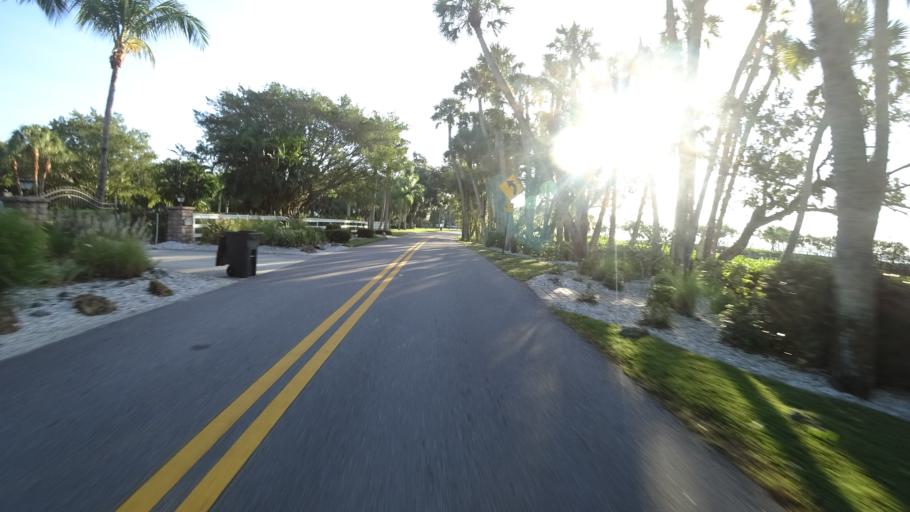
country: US
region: Florida
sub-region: Manatee County
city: Memphis
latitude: 27.5704
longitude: -82.5761
